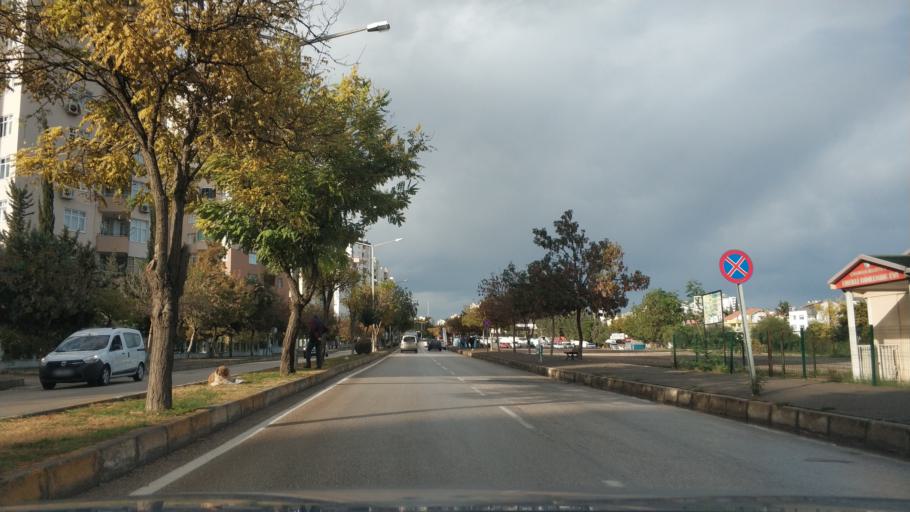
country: TR
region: Adana
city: Seyhan
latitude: 37.0388
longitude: 35.2613
